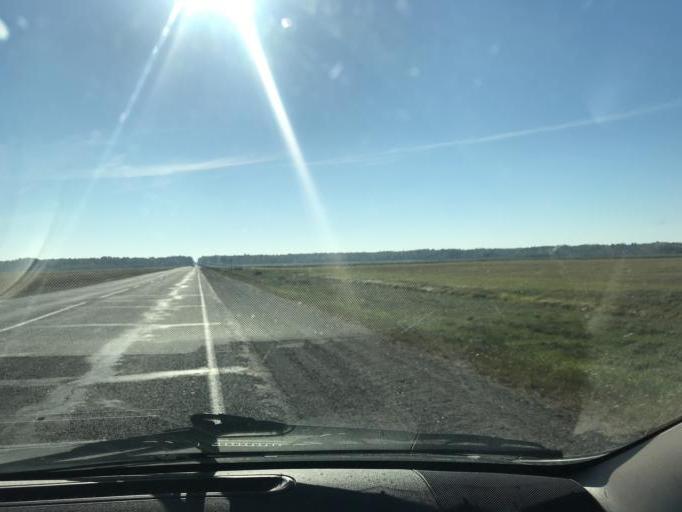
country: BY
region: Minsk
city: Starobin
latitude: 52.5200
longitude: 27.4742
